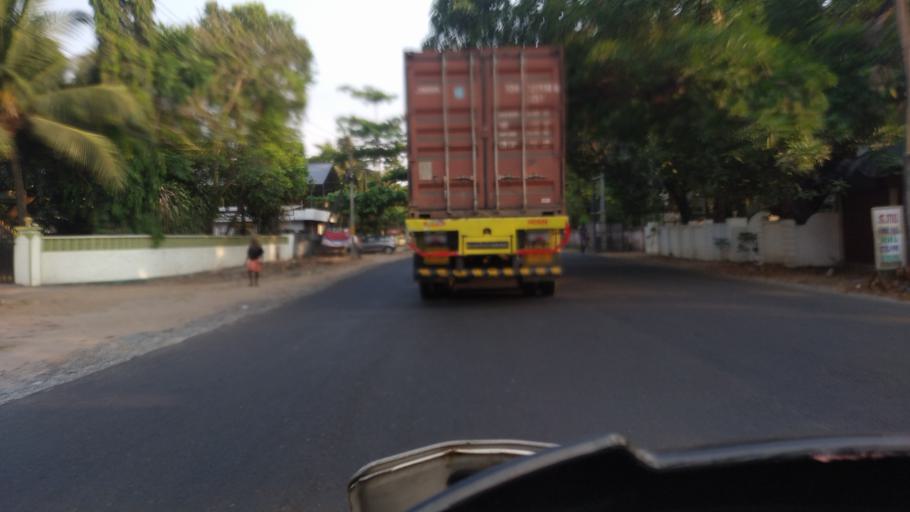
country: IN
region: Kerala
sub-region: Thrissur District
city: Thanniyam
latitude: 10.3926
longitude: 76.1176
